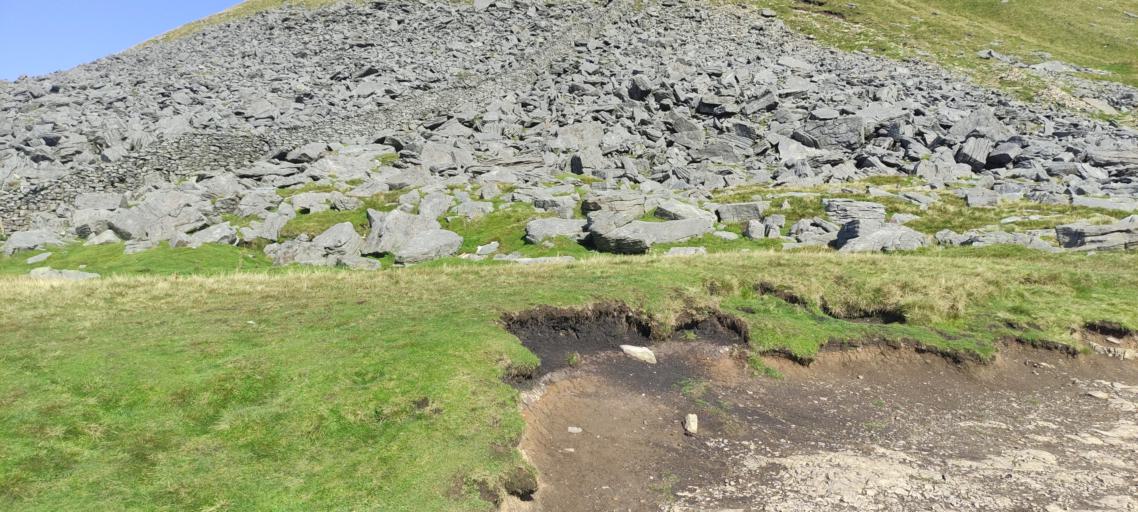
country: GB
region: England
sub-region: North Yorkshire
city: Settle
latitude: 54.1518
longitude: -2.2514
